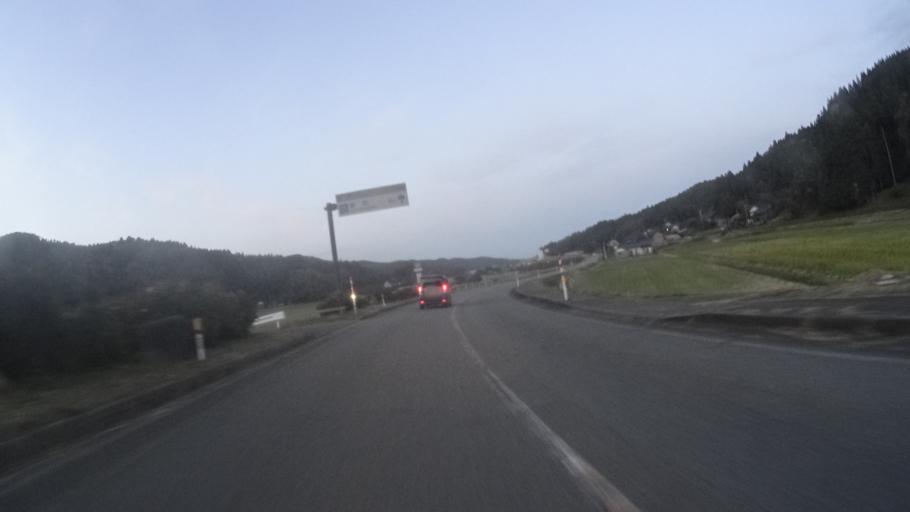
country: JP
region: Ishikawa
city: Nanao
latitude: 37.3608
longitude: 136.8658
